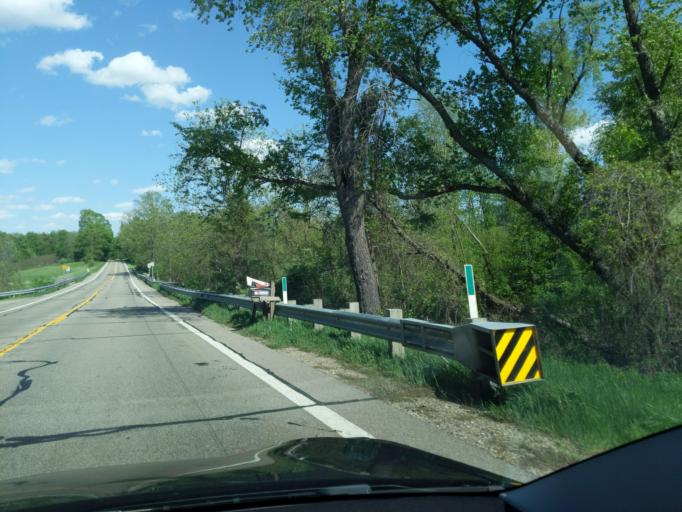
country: US
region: Michigan
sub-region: Kent County
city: Lowell
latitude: 42.7986
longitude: -85.3367
